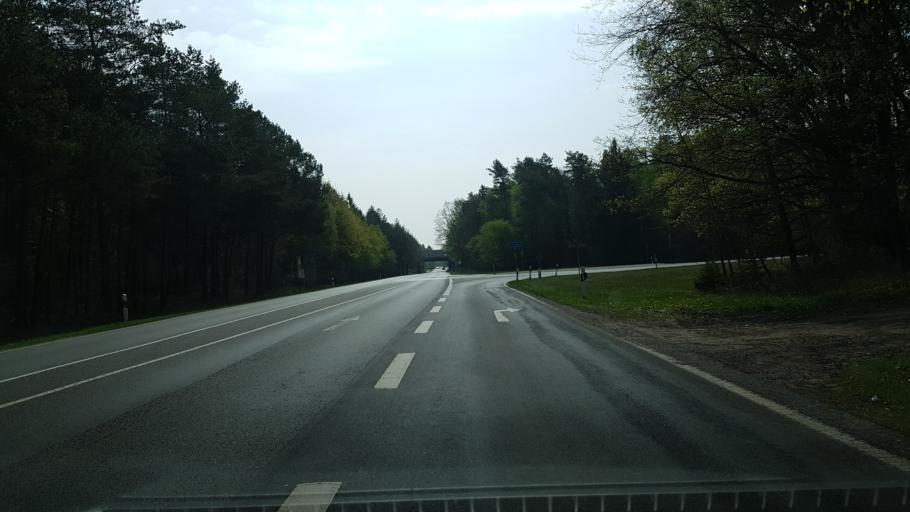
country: DE
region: Lower Saxony
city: Soltau
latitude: 52.9503
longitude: 9.8726
